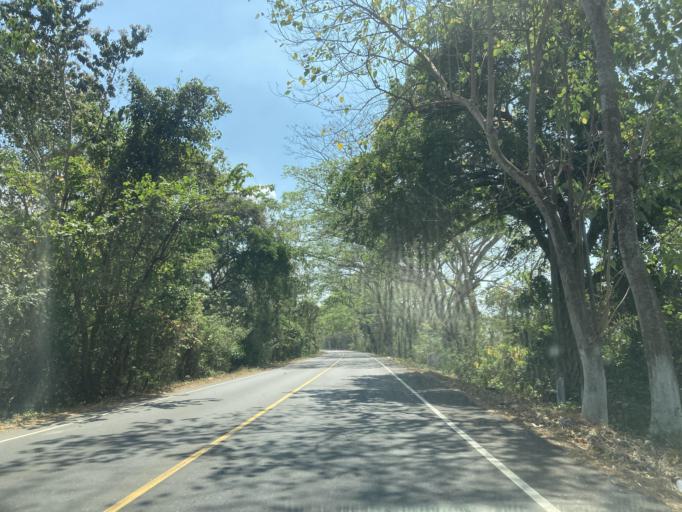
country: GT
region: Escuintla
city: Guanagazapa
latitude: 14.1806
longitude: -90.6887
